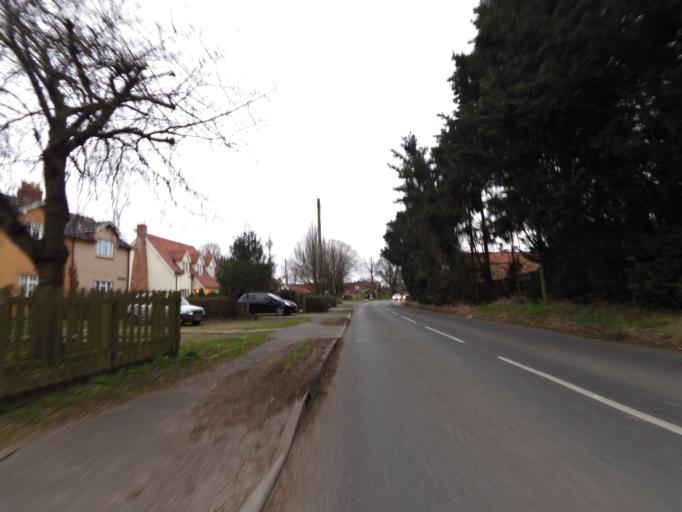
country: GB
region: England
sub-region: Suffolk
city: Ipswich
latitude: 52.1189
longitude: 1.1498
